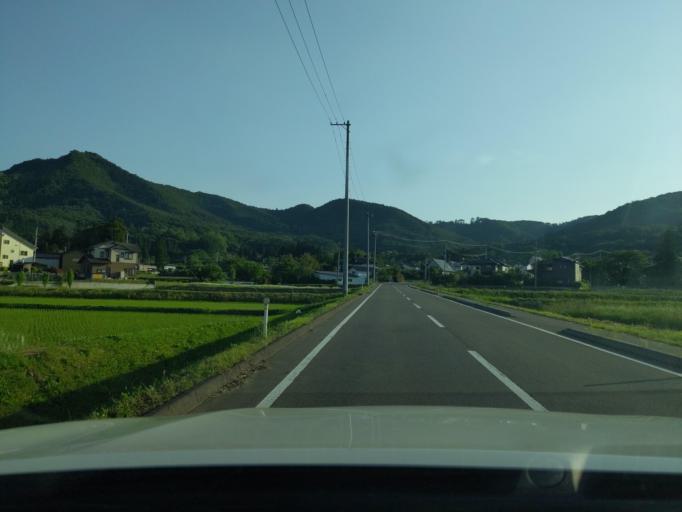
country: JP
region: Fukushima
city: Motomiya
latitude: 37.5275
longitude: 140.3593
